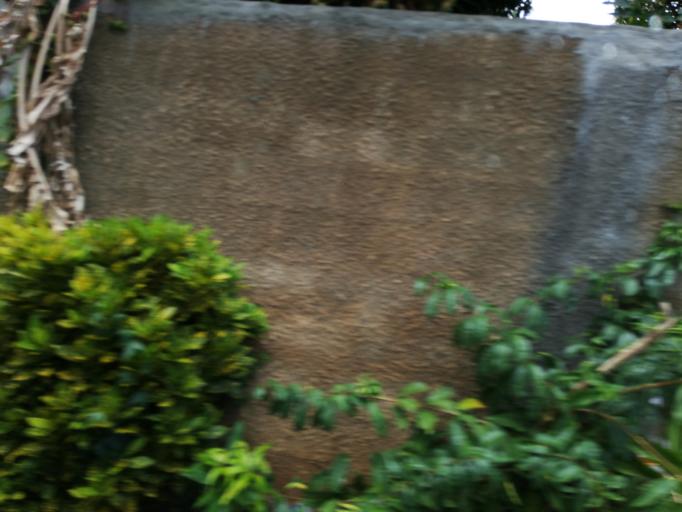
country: MU
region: Moka
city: Moka
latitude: -20.2157
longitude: 57.4742
